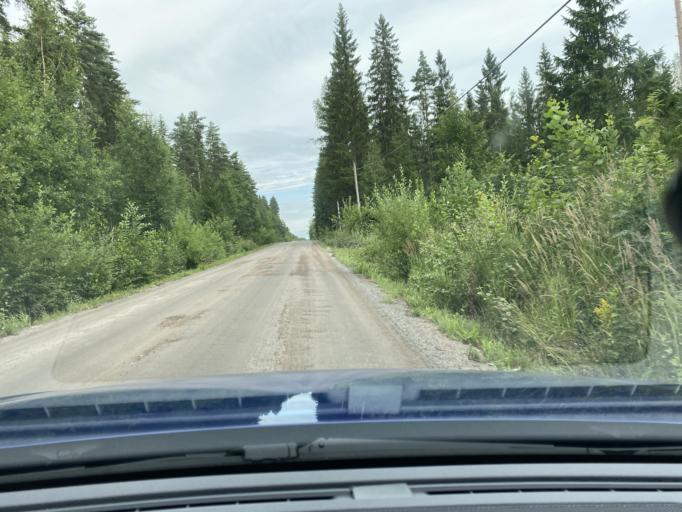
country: FI
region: Satakunta
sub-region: Rauma
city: Kiukainen
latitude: 61.1358
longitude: 21.9899
